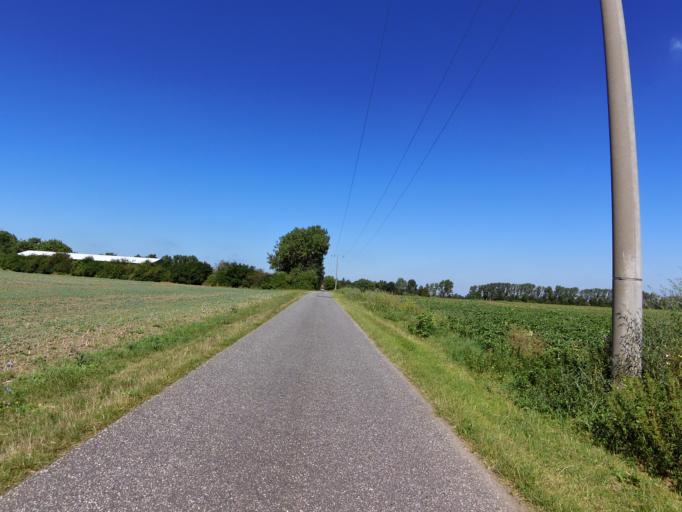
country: DE
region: Brandenburg
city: Muhlberg
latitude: 51.4042
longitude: 13.2257
